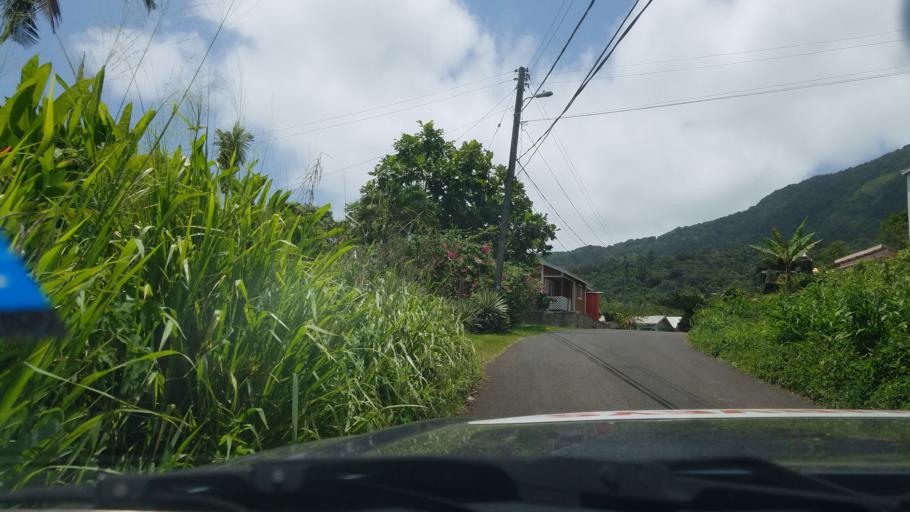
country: LC
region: Castries Quarter
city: Bisee
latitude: 13.9894
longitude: -60.9237
